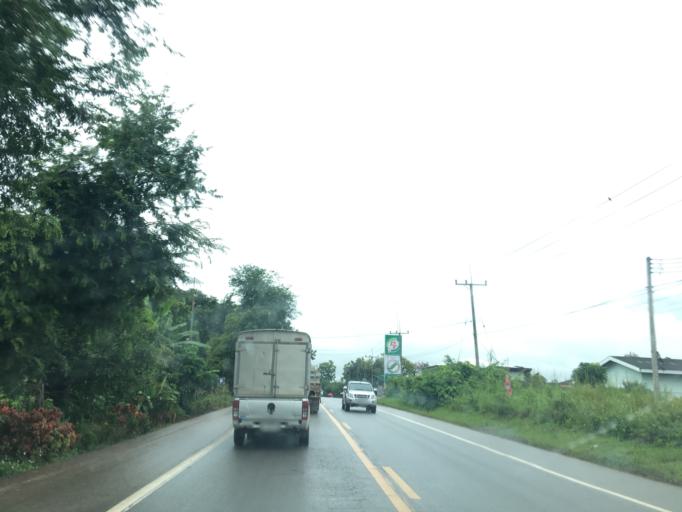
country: TH
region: Chiang Rai
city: Wiang Chai
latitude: 19.7901
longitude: 99.9093
